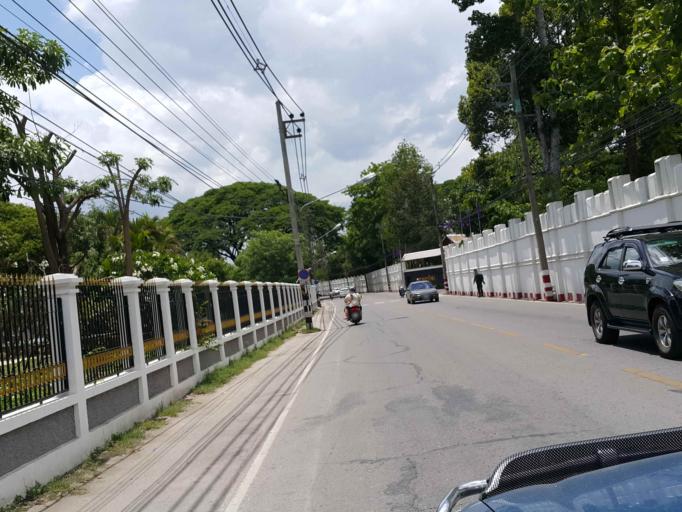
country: TH
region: Chiang Mai
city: Chiang Mai
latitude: 18.7781
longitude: 99.0078
